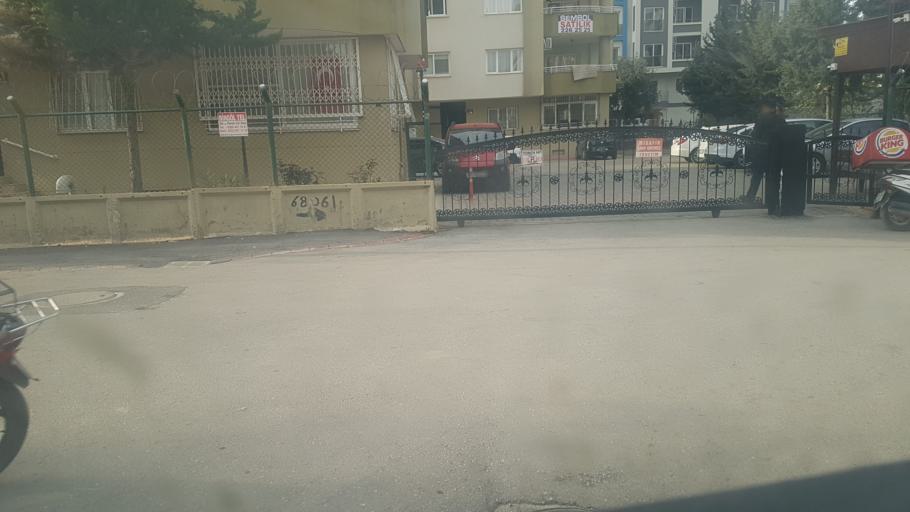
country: TR
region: Adana
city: Adana
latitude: 37.0258
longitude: 35.3175
